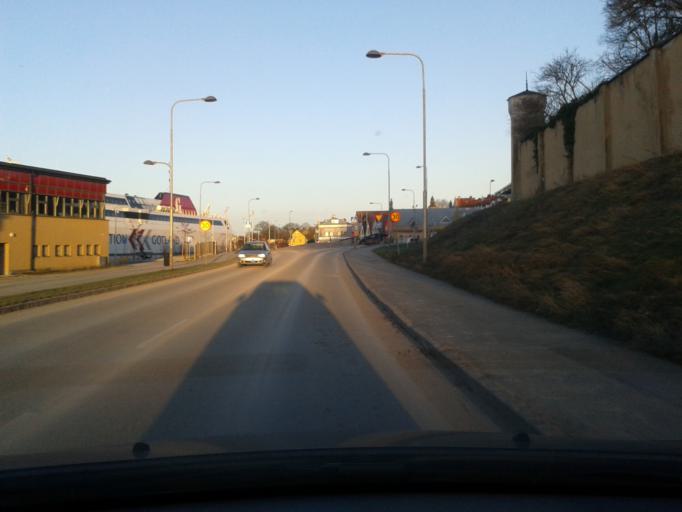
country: SE
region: Gotland
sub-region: Gotland
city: Visby
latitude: 57.6360
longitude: 18.2850
